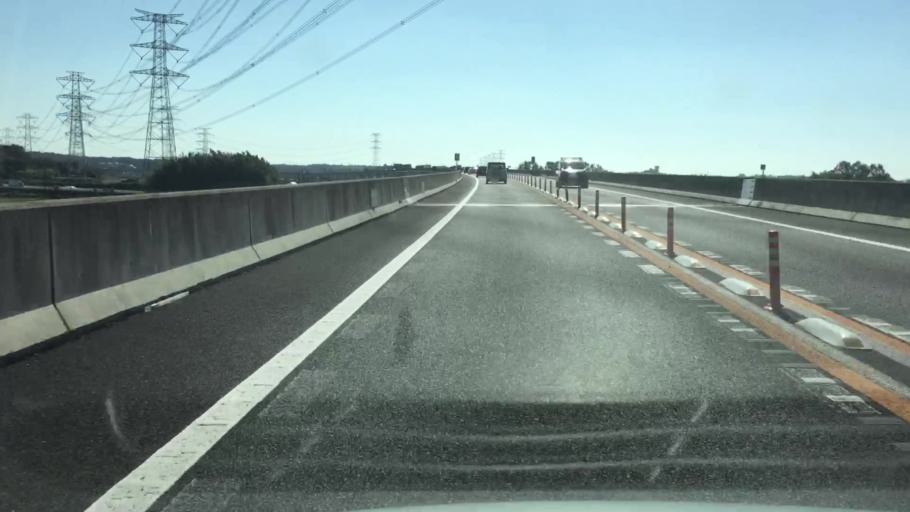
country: JP
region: Ibaraki
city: Ushiku
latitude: 36.0000
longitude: 140.1488
